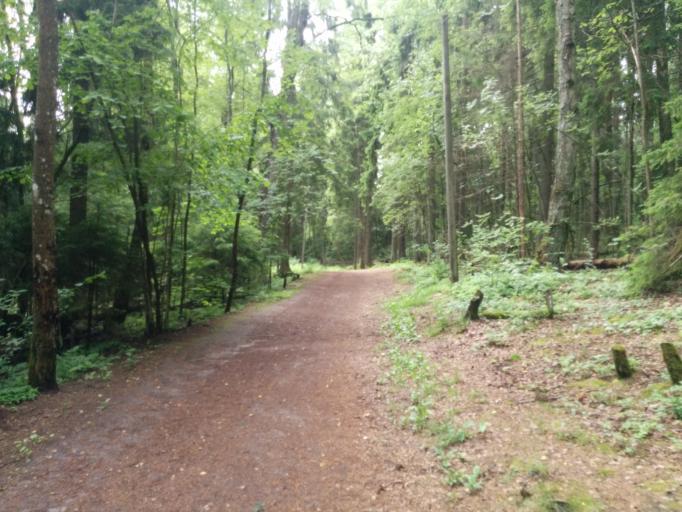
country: FI
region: Uusimaa
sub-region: Helsinki
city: Vantaa
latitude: 60.2402
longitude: 25.1280
